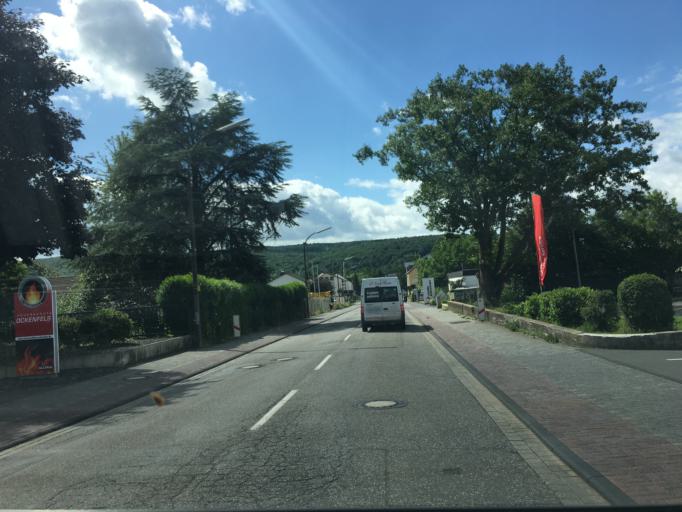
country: DE
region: Rheinland-Pfalz
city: Bad Neuenahr-Ahrweiler
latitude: 50.5493
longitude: 7.1195
